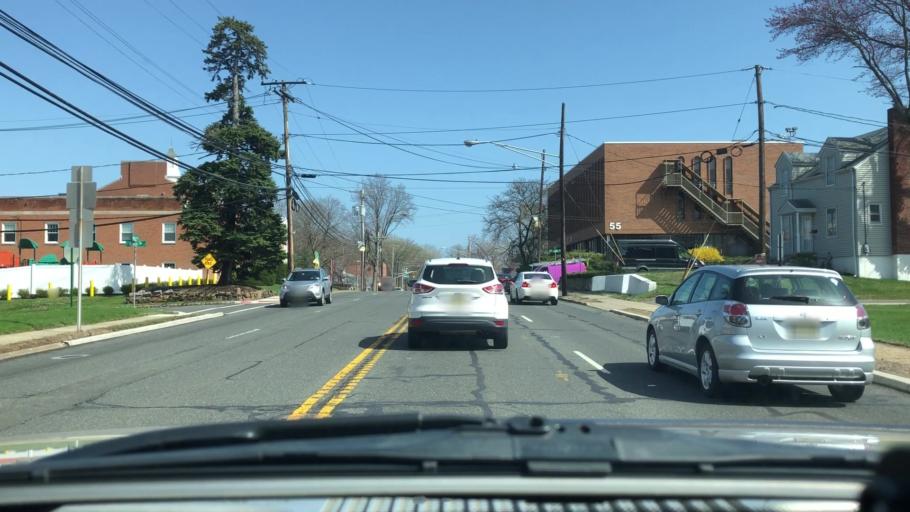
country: US
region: New Jersey
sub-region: Union County
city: Springfield
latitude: 40.7093
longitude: -74.3053
